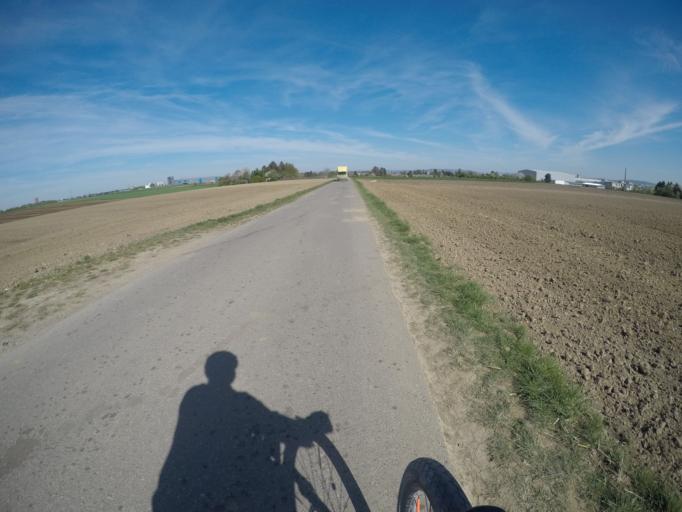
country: DE
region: Baden-Wuerttemberg
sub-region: Regierungsbezirk Stuttgart
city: Kornwestheim
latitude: 48.8683
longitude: 9.1651
